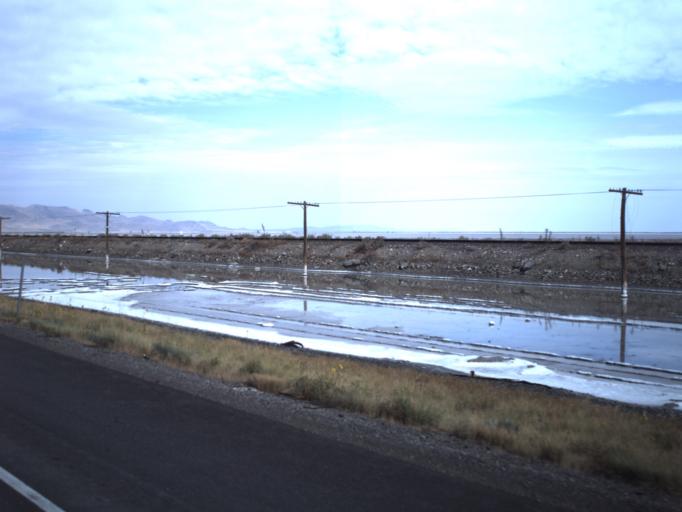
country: US
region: Utah
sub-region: Tooele County
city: Grantsville
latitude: 40.7297
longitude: -112.5861
